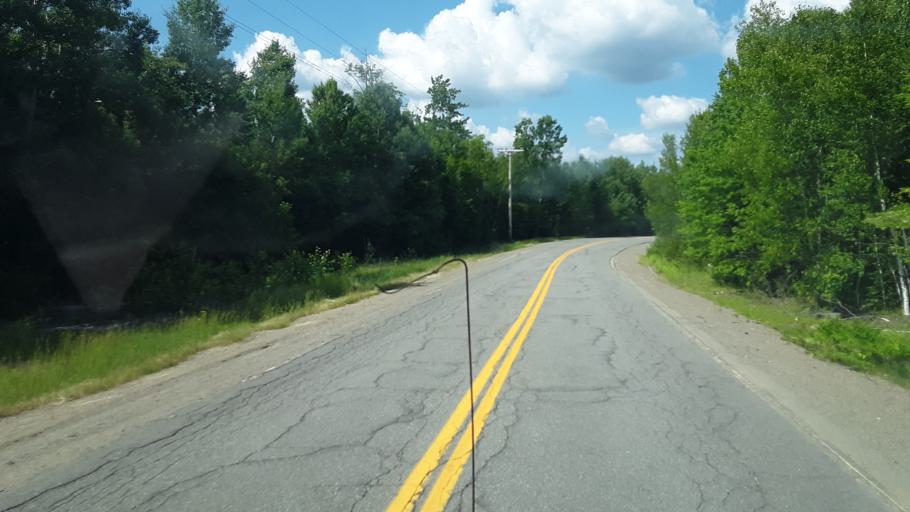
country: US
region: Maine
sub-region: Washington County
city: Calais
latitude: 45.1123
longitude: -67.5068
